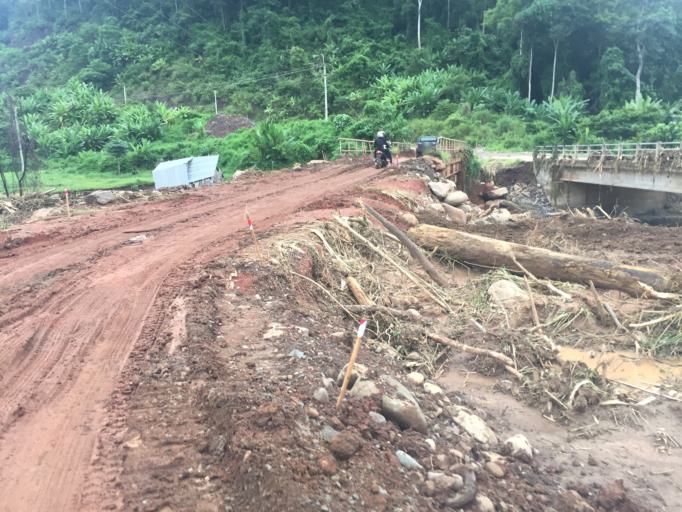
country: LA
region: Xekong
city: Lamam
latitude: 15.1269
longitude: 106.6721
